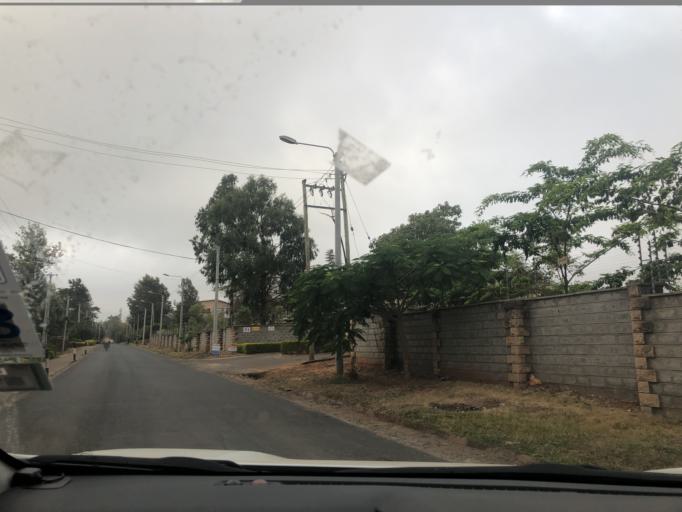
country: KE
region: Nairobi Area
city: Pumwani
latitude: -1.2298
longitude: 36.8588
